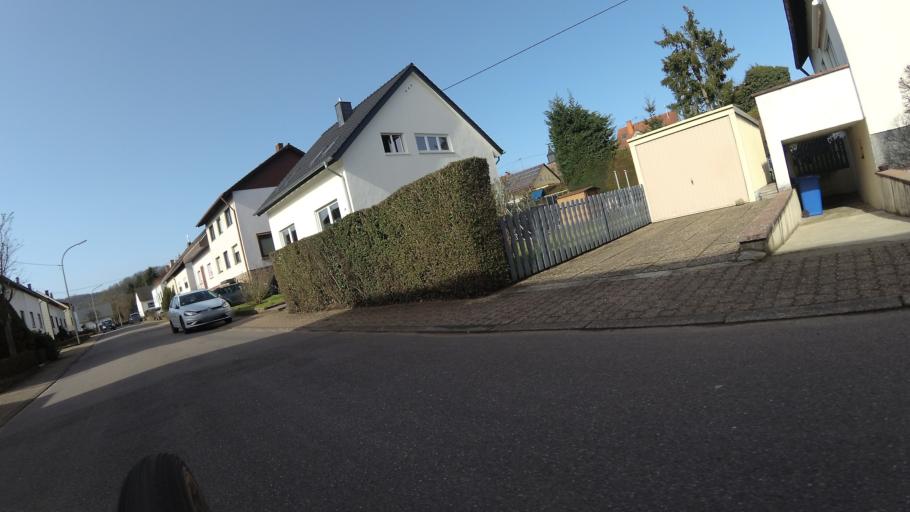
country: DE
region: Saarland
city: Uberherrn
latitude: 49.2736
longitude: 6.7060
